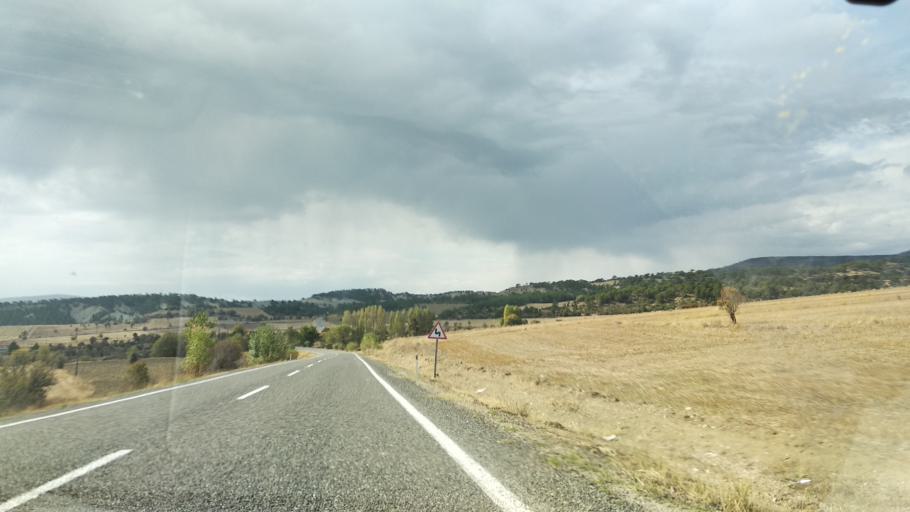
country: TR
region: Bolu
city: Seben
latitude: 40.3660
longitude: 31.4993
